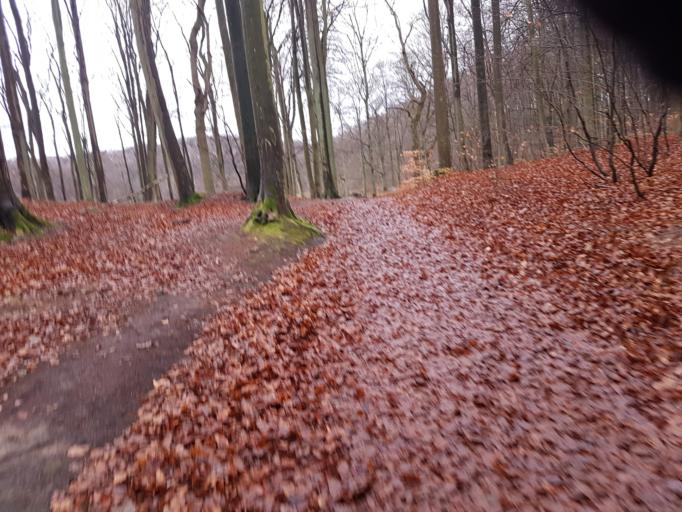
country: DE
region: Mecklenburg-Vorpommern
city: Ostseebad Sellin
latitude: 54.3951
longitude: 13.6703
